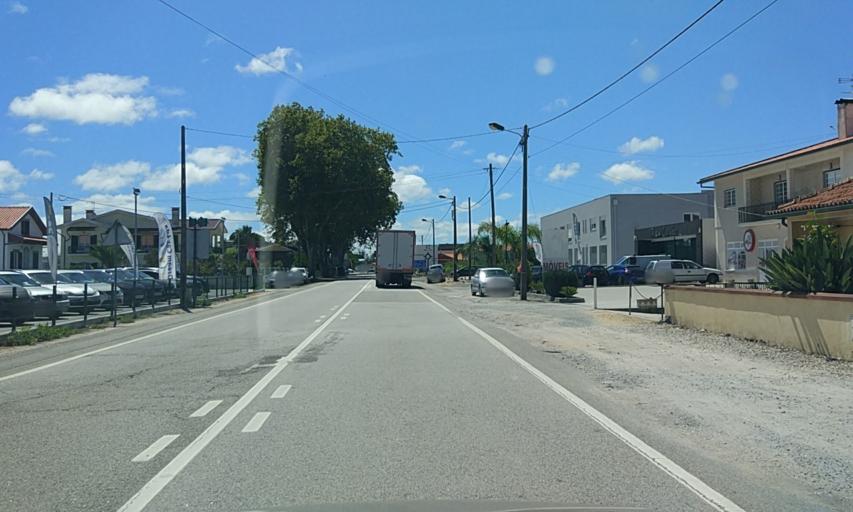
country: PT
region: Coimbra
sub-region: Mira
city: Mira
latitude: 40.4623
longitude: -8.7009
